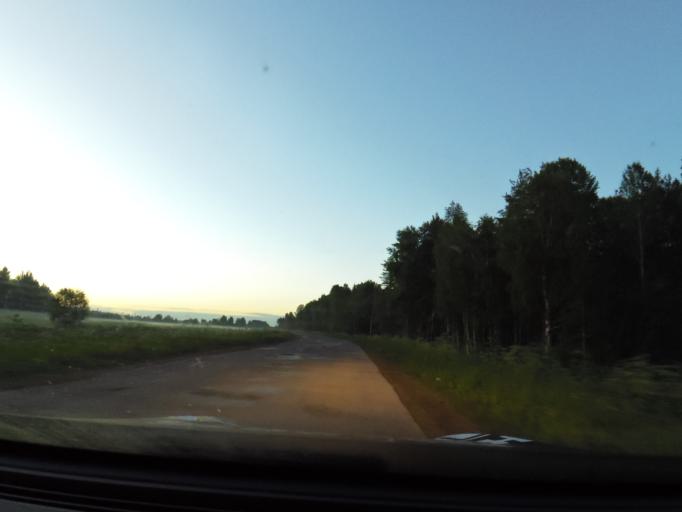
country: RU
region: Vologda
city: Vytegra
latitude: 60.9950
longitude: 36.3736
